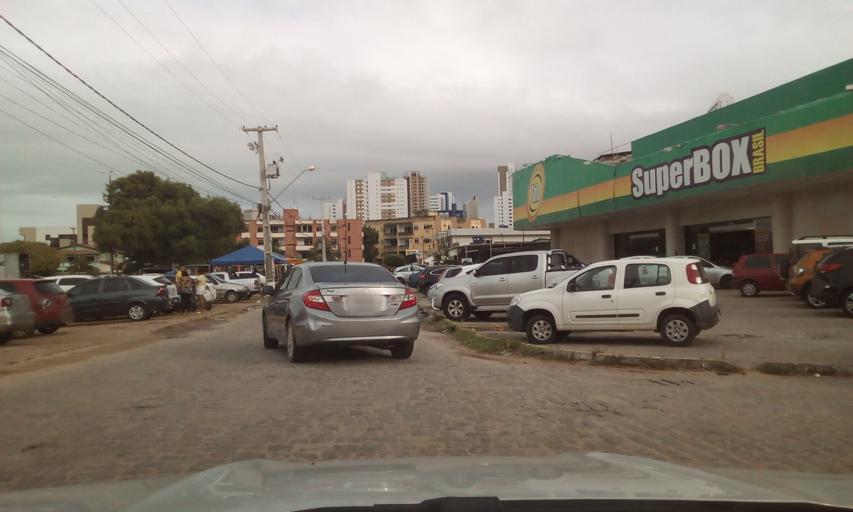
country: BR
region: Paraiba
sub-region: Joao Pessoa
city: Joao Pessoa
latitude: -7.0760
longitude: -34.8391
